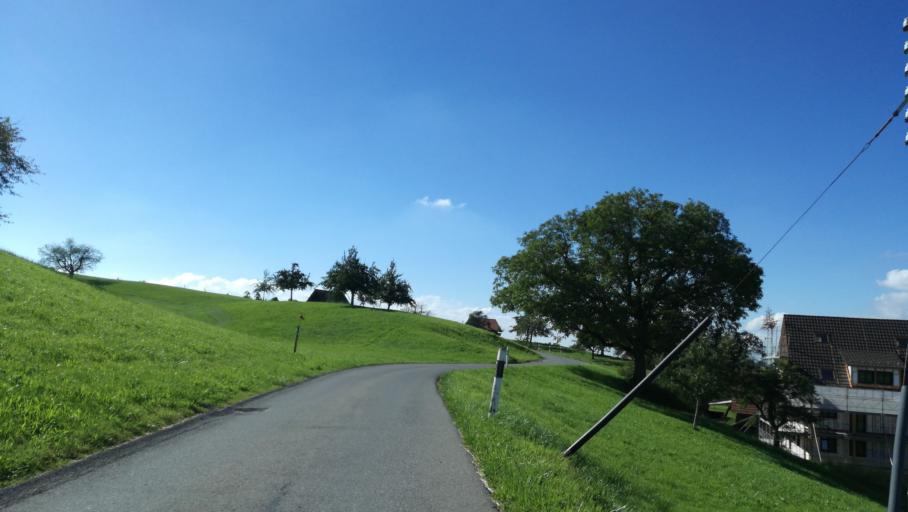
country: CH
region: Zug
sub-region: Zug
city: Zug
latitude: 47.1618
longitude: 8.5449
